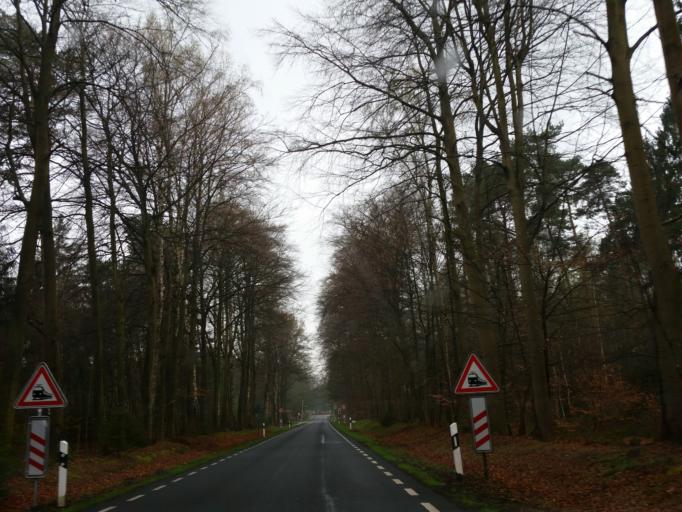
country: DE
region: Lower Saxony
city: Hipstedt
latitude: 53.5008
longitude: 8.9734
